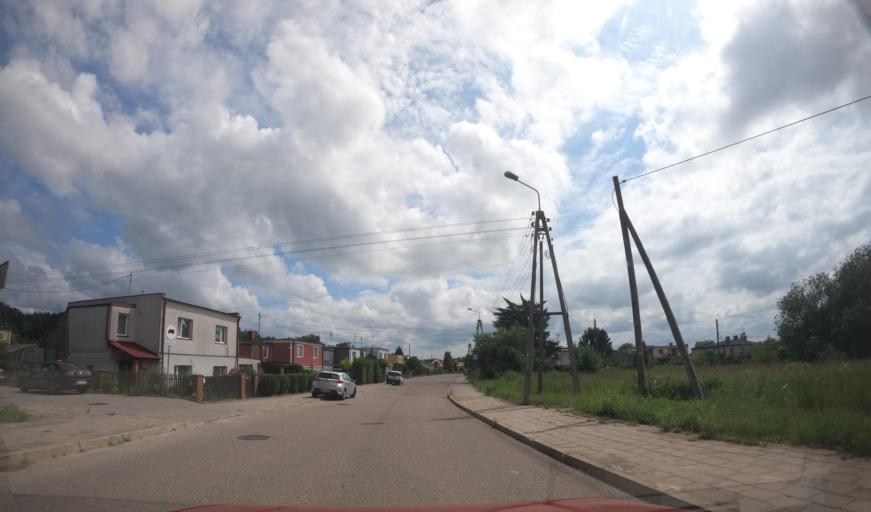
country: PL
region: West Pomeranian Voivodeship
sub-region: Powiat koszalinski
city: Sianow
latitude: 54.1923
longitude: 16.2368
